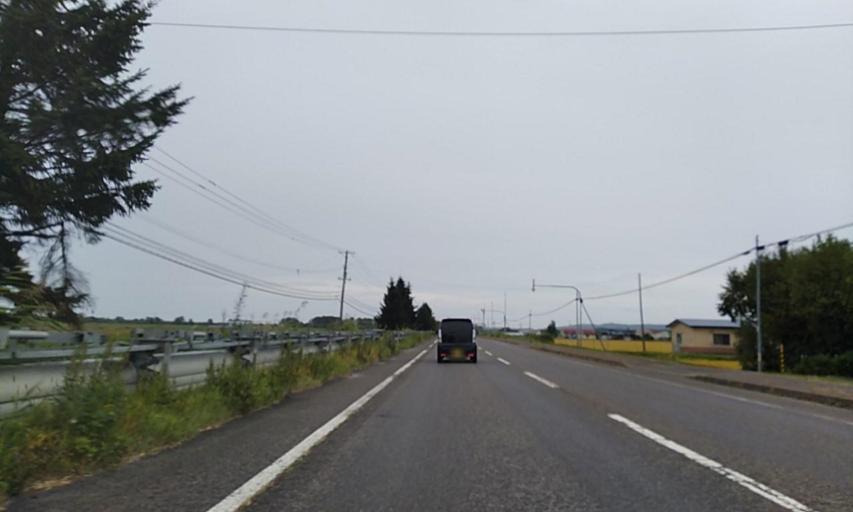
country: JP
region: Hokkaido
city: Bihoro
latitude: 43.9118
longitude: 144.1553
